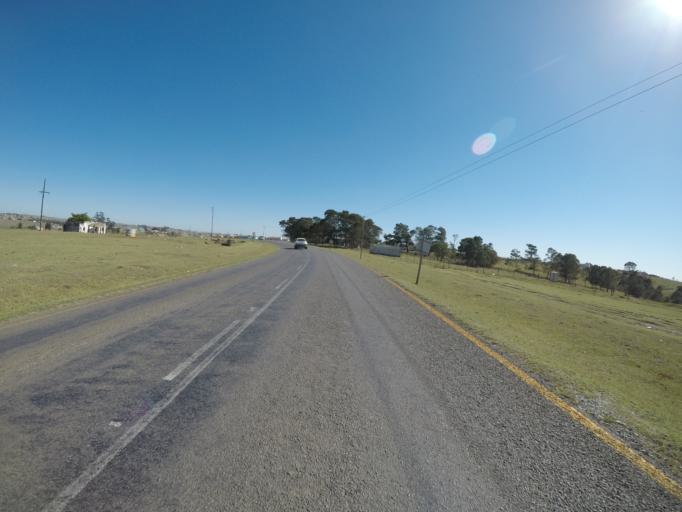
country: ZA
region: Eastern Cape
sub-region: OR Tambo District Municipality
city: Mthatha
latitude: -31.7917
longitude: 28.7452
